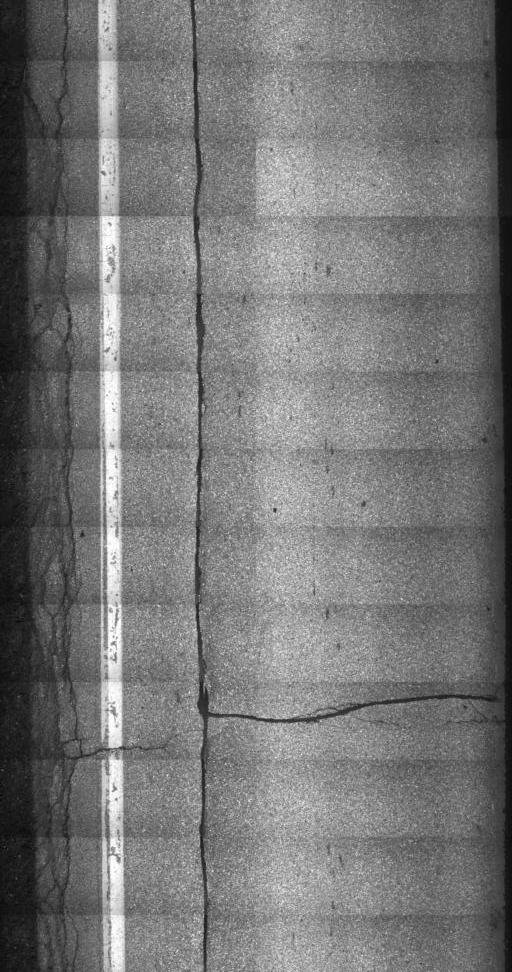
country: US
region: Vermont
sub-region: Chittenden County
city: Milton
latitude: 44.6644
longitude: -73.1115
